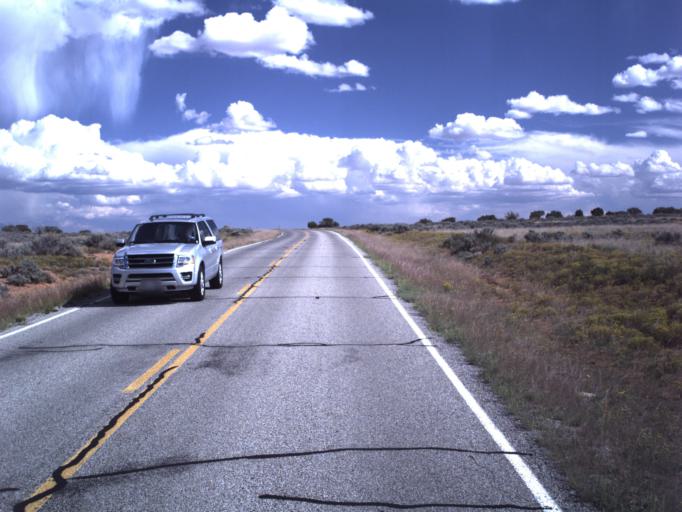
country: US
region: Utah
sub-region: Grand County
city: Moab
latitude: 38.5239
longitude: -109.7429
